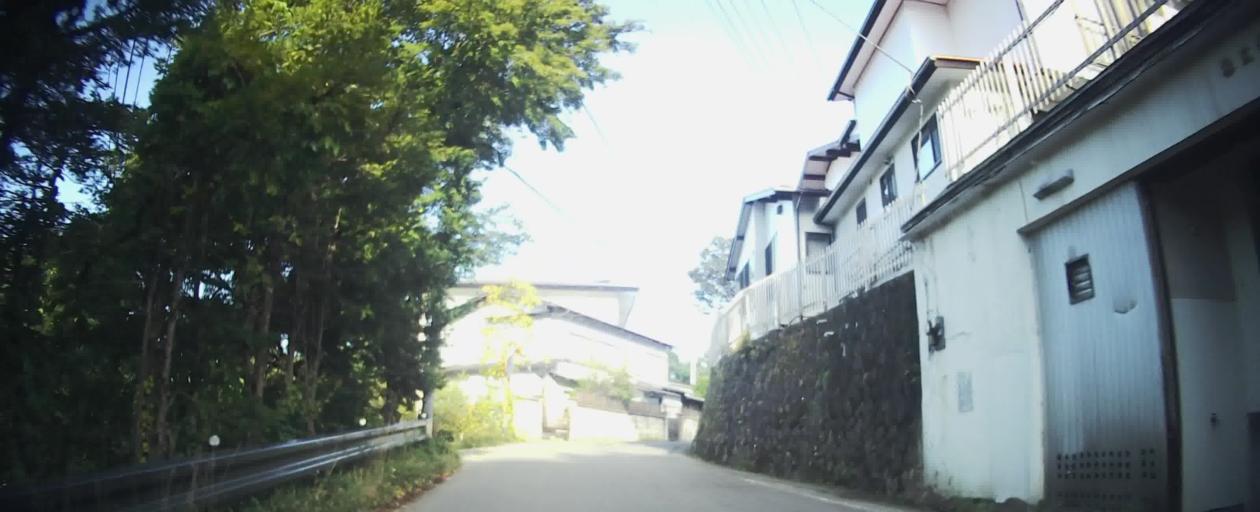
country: JP
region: Gunma
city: Nakanojomachi
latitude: 36.6226
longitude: 138.6020
